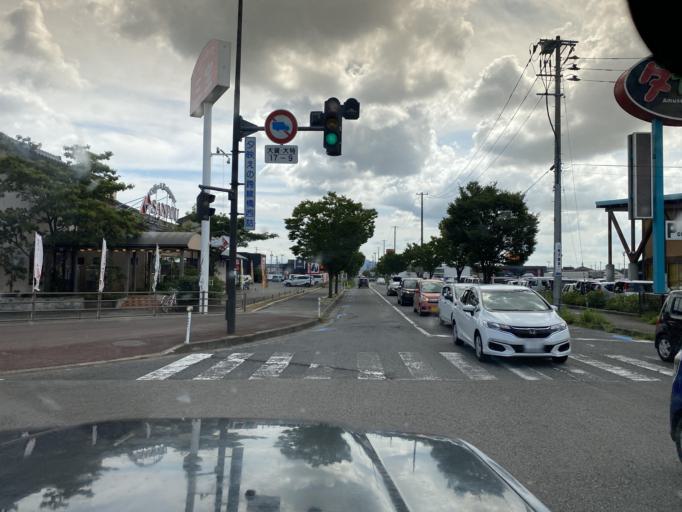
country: JP
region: Niigata
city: Niitsu-honcho
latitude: 37.8066
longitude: 139.1152
